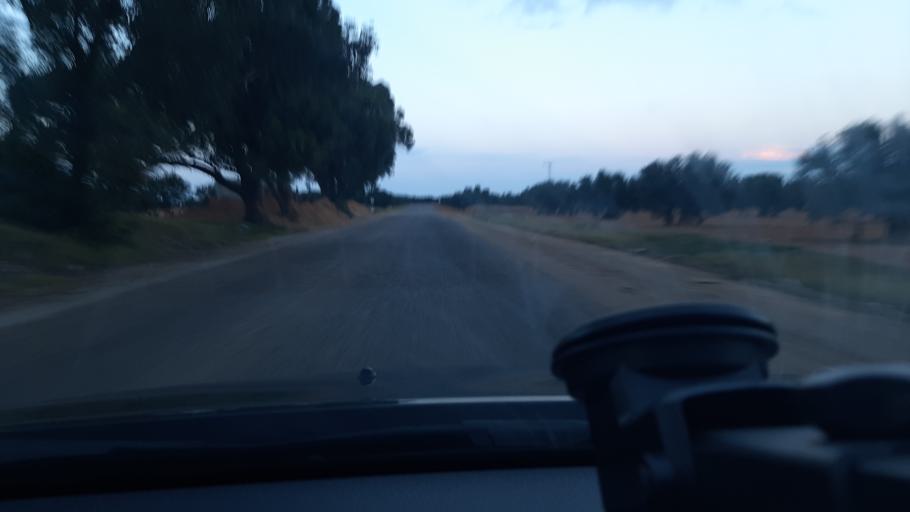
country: TN
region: Al Mahdiyah
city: Shurban
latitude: 34.9825
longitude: 10.3854
